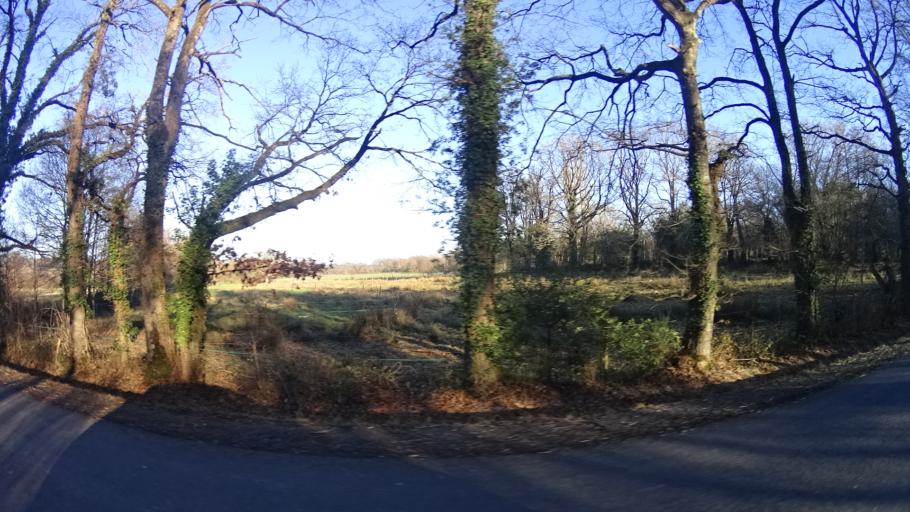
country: FR
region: Brittany
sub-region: Departement du Morbihan
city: Allaire
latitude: 47.6713
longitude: -2.1730
